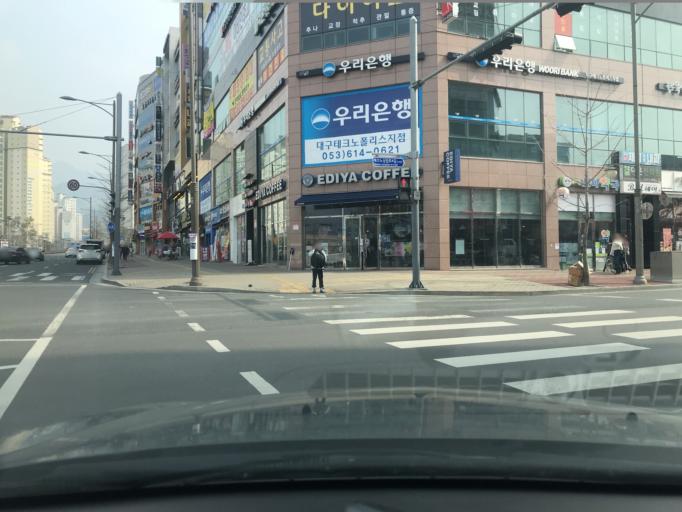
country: KR
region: Daegu
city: Hwawon
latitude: 35.6935
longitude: 128.4607
